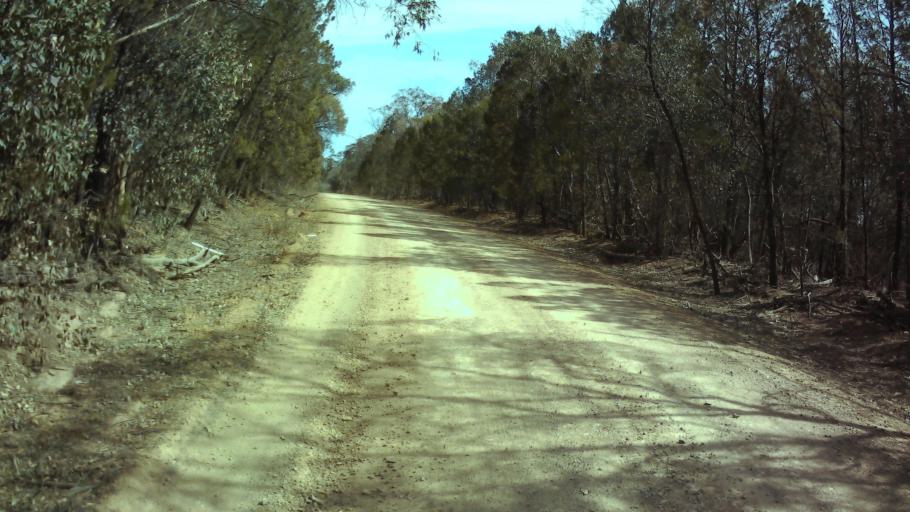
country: AU
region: New South Wales
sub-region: Weddin
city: Grenfell
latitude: -33.8817
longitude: 148.1512
